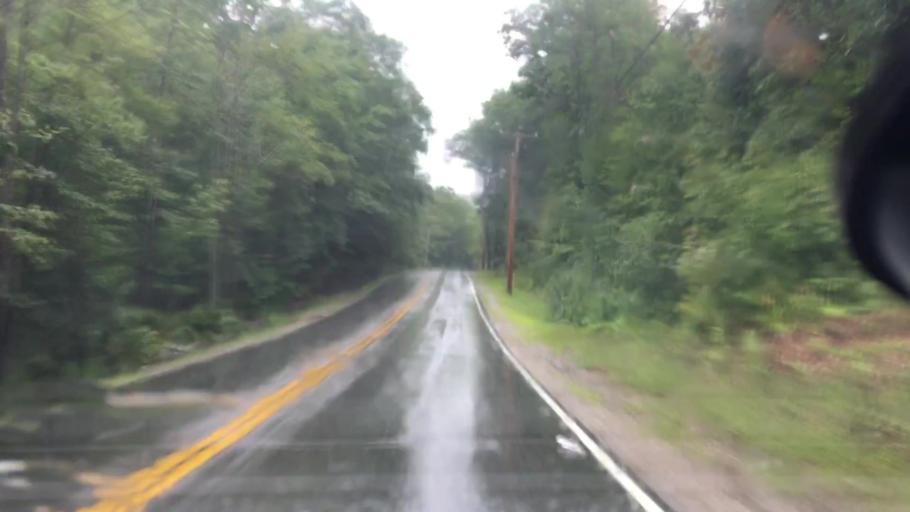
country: US
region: Maine
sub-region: Oxford County
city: Lovell
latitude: 44.2585
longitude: -70.8351
